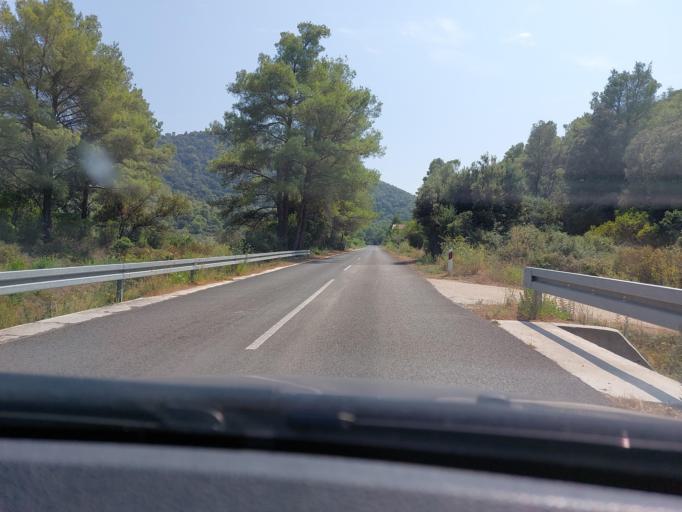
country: HR
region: Dubrovacko-Neretvanska
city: Smokvica
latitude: 42.7517
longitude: 16.8359
